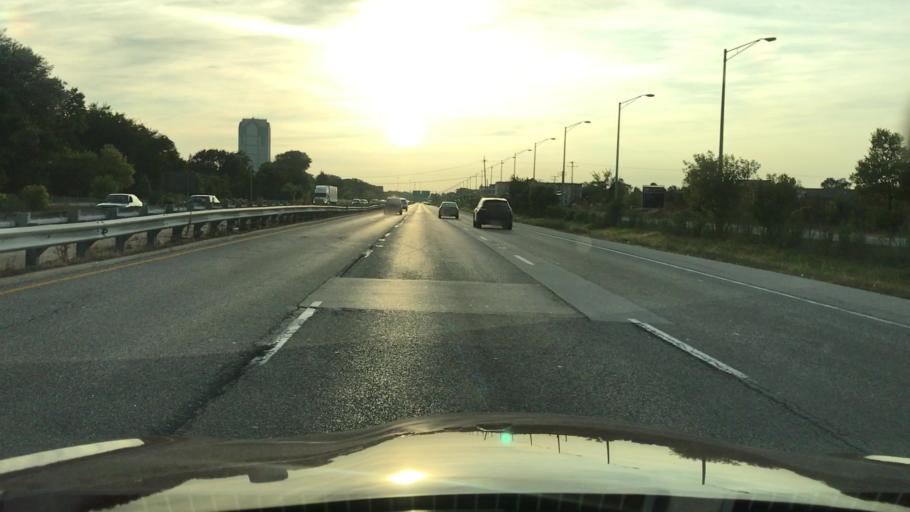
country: US
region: Illinois
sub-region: DuPage County
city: Oak Brook
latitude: 41.8614
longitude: -87.9360
